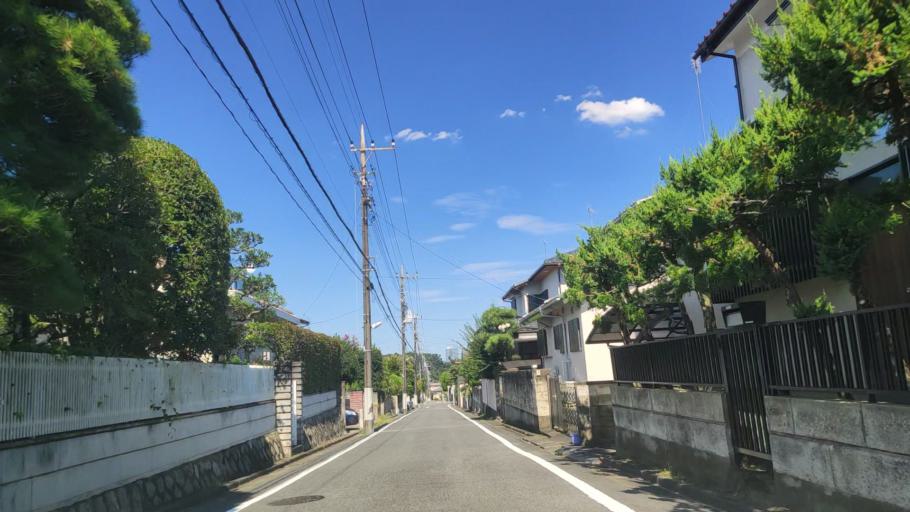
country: JP
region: Tokyo
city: Hachioji
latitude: 35.6453
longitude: 139.3082
